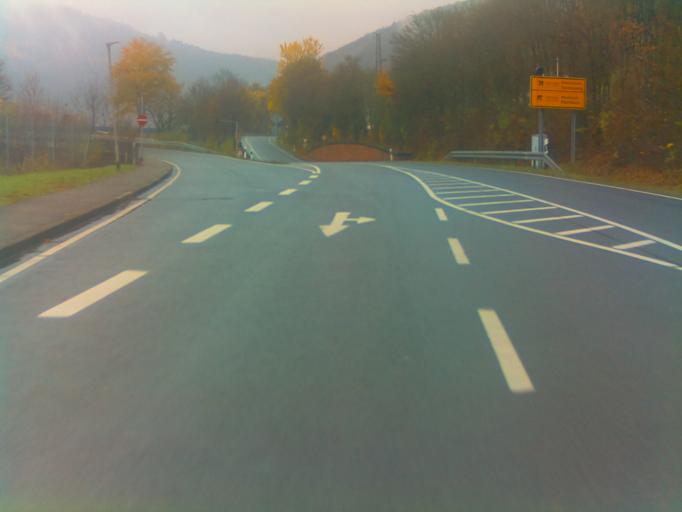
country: DE
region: Hesse
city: Hirschhorn
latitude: 49.4386
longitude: 8.8960
